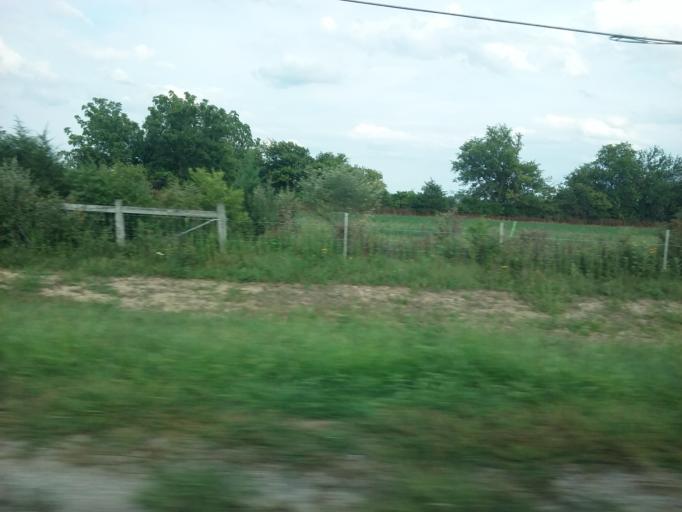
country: US
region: Ohio
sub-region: Wood County
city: Bowling Green
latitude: 41.3331
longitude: -83.6503
